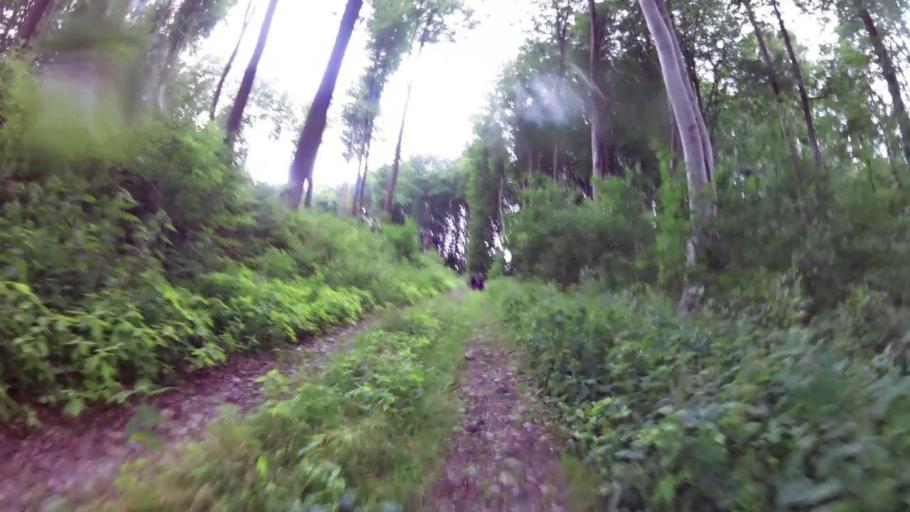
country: PL
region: West Pomeranian Voivodeship
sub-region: Powiat lobeski
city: Lobez
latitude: 53.7600
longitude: 15.5877
